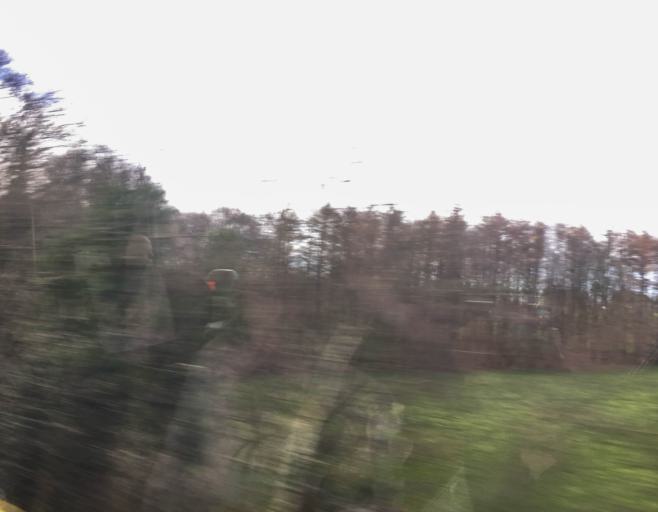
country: GB
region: Scotland
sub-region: Dumfries and Galloway
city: Lockerbie
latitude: 55.1010
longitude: -3.3282
